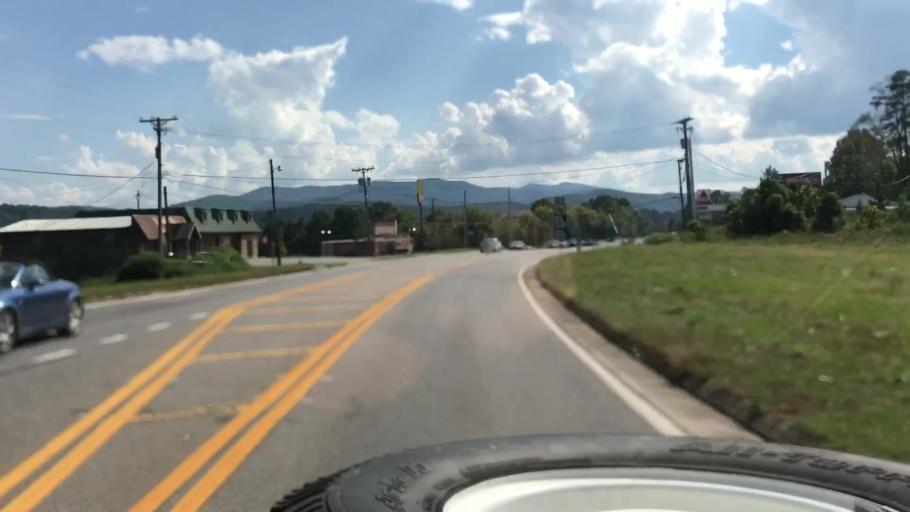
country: US
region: Georgia
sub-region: Fannin County
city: Blue Ridge
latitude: 34.8759
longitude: -84.3221
